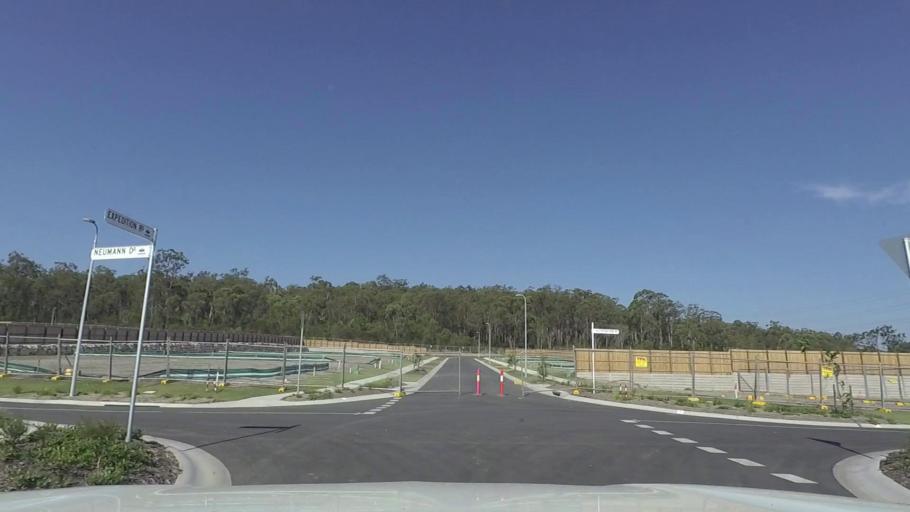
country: AU
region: Queensland
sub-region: Logan
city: Chambers Flat
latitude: -27.8171
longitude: 153.1319
